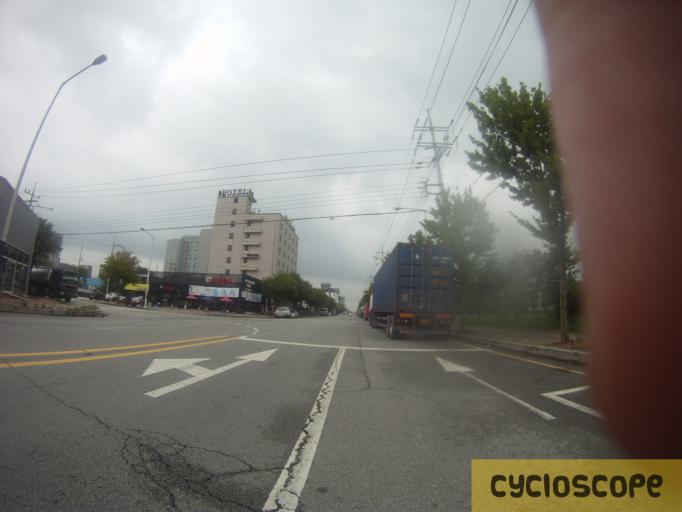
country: KR
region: Gyeonggi-do
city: Hwaseong-si
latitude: 37.0806
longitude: 126.7984
